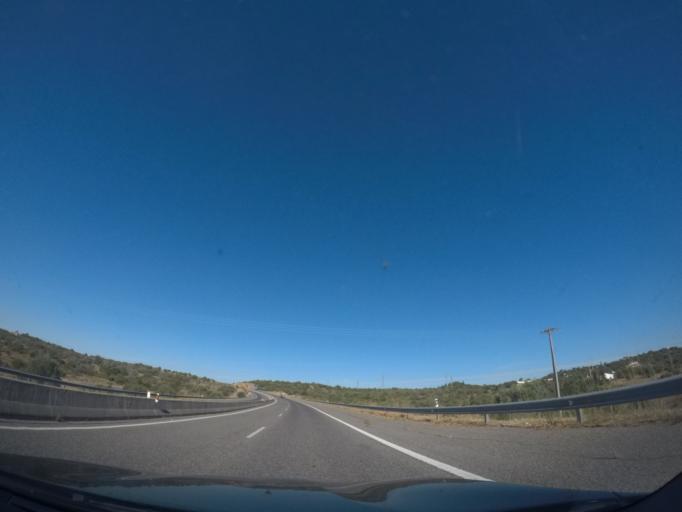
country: PT
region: Faro
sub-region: Portimao
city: Alvor
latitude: 37.1835
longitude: -8.5934
